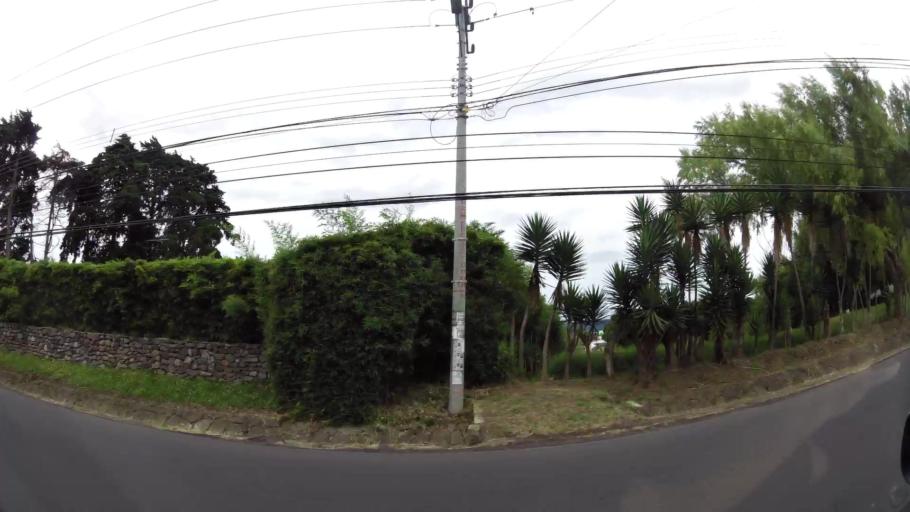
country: CR
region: San Jose
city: Ipis
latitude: 9.9679
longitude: -84.0207
